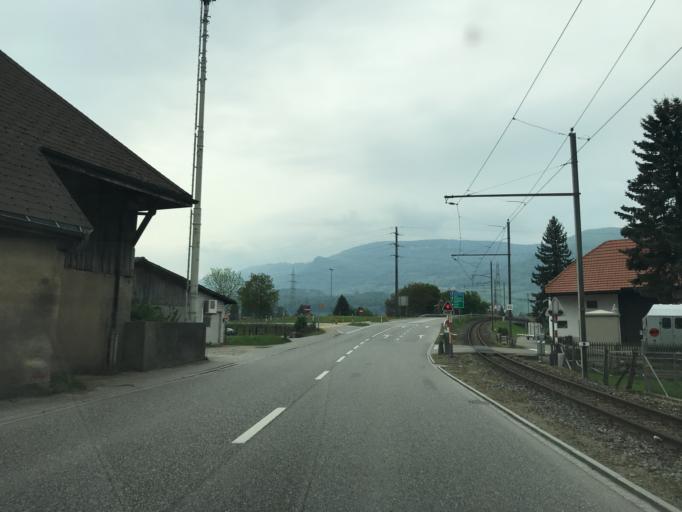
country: CH
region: Bern
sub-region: Oberaargau
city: Niederbipp
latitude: 47.2594
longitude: 7.7081
